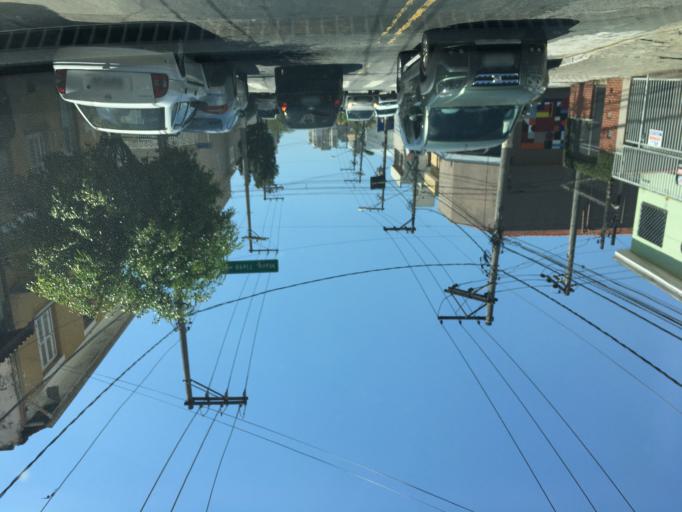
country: BR
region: Sao Paulo
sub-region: Sao Paulo
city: Sao Paulo
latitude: -23.5370
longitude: -46.5838
